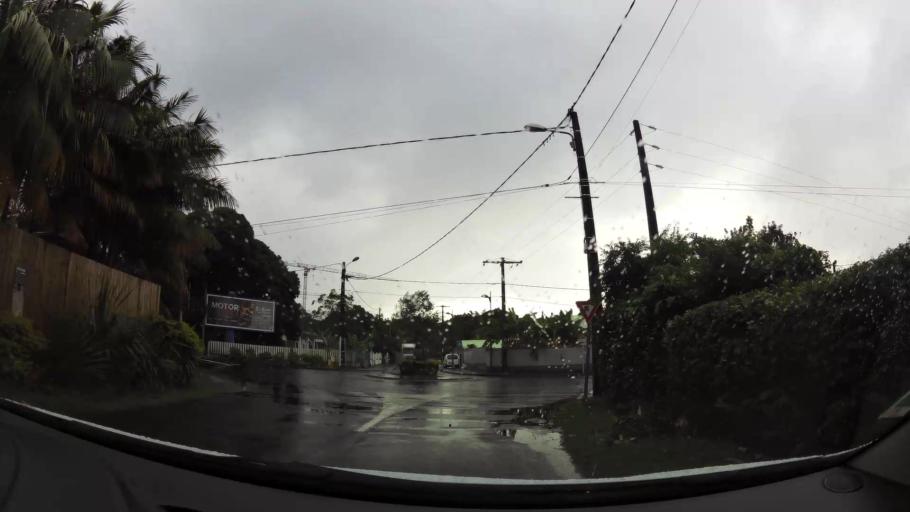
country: RE
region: Reunion
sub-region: Reunion
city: Saint-Andre
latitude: -20.9728
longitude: 55.6520
